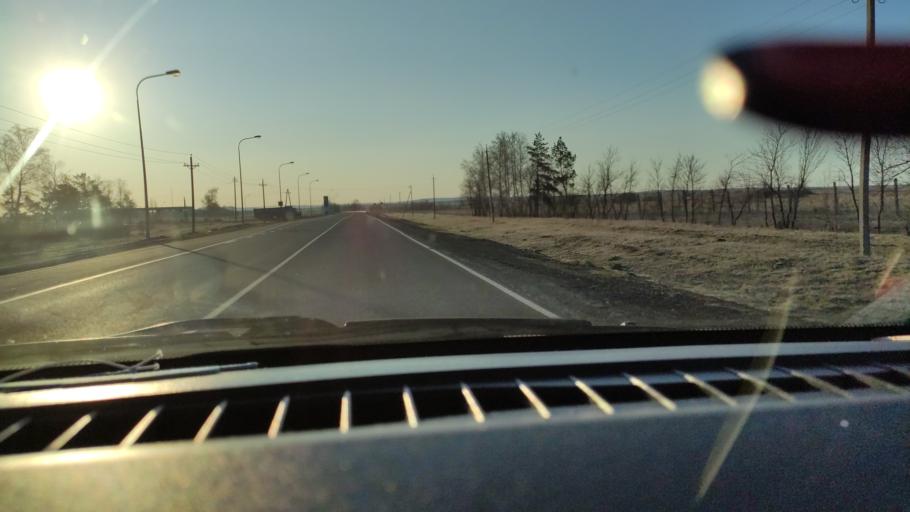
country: RU
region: Saratov
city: Sennoy
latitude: 52.1505
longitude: 46.9755
